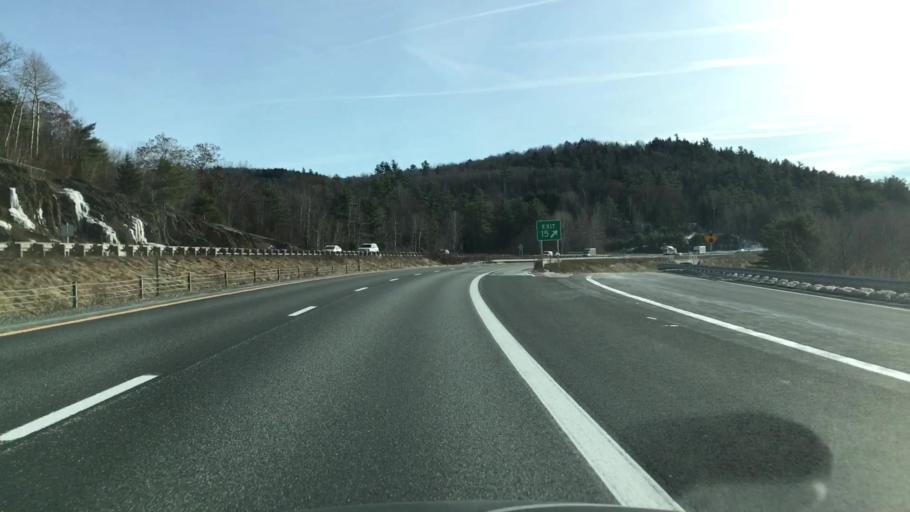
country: US
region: New Hampshire
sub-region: Grafton County
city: Enfield
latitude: 43.5996
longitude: -72.1668
